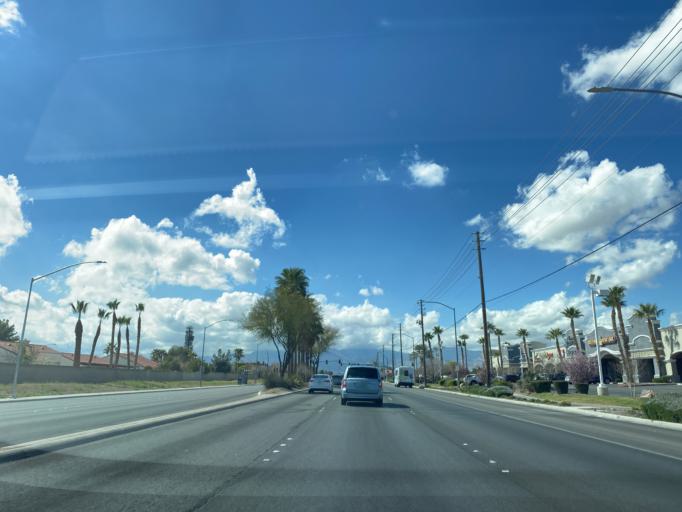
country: US
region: Nevada
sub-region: Clark County
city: Las Vegas
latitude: 36.2392
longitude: -115.1961
